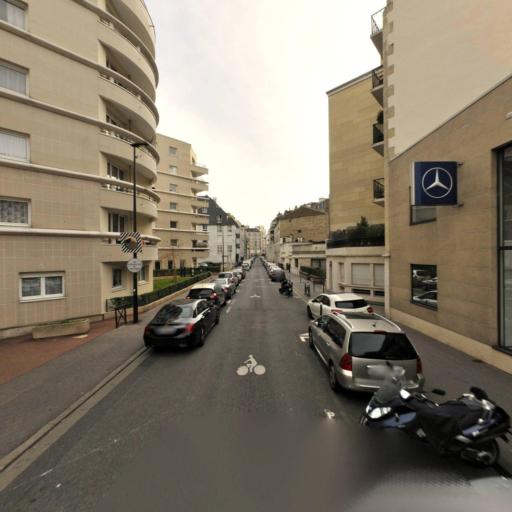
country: FR
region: Ile-de-France
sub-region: Departement des Hauts-de-Seine
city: Boulogne-Billancourt
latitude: 48.8395
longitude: 2.2484
